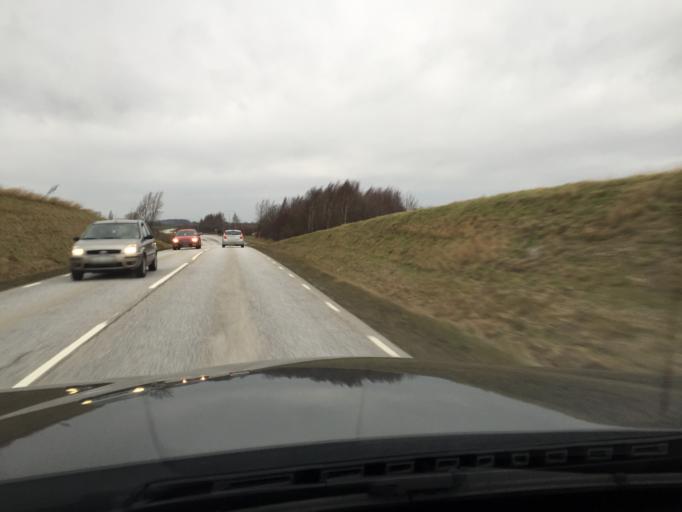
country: SE
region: Skane
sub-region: Malmo
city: Oxie
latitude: 55.5826
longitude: 13.1377
